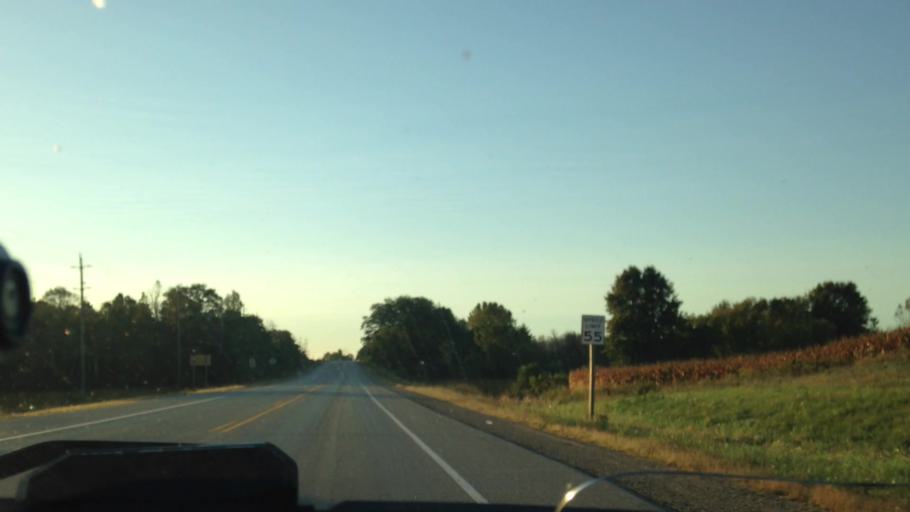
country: US
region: Wisconsin
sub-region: Ozaukee County
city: Saukville
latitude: 43.3956
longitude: -87.9787
